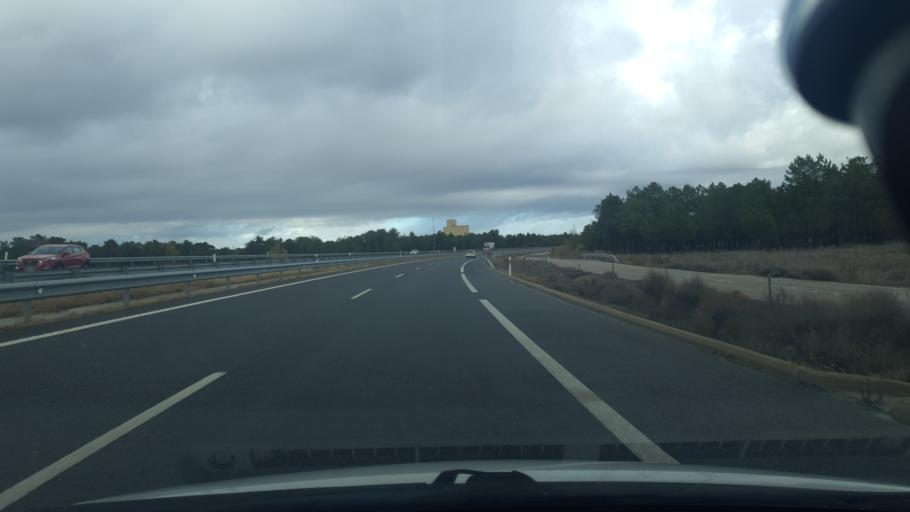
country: ES
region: Castille and Leon
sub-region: Provincia de Segovia
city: Sanchonuno
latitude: 41.3264
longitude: -4.3136
